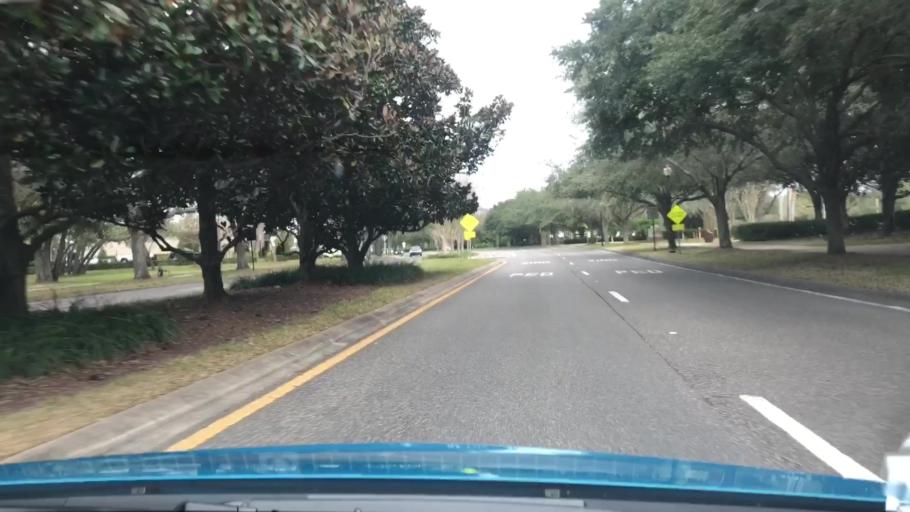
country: US
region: Florida
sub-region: Seminole County
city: Heathrow
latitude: 28.7775
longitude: -81.3579
